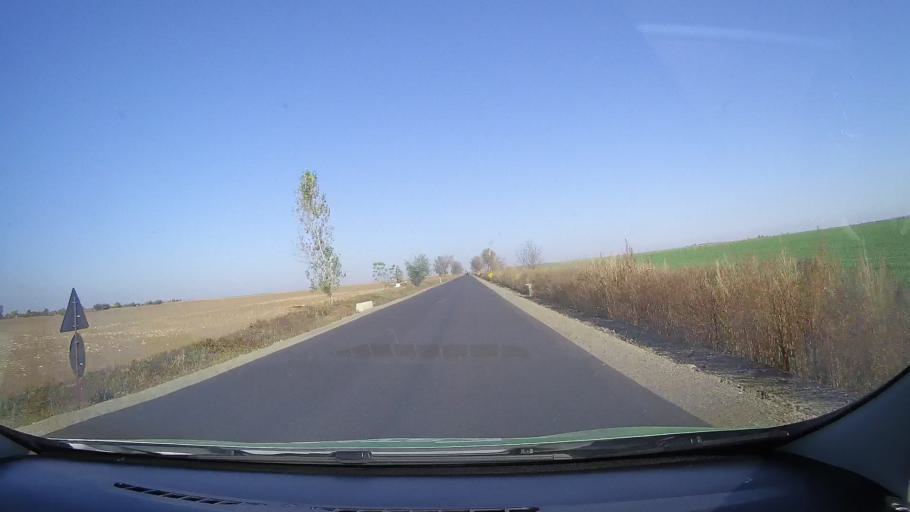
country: RO
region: Satu Mare
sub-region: Comuna Tiream
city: Tiream
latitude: 47.6241
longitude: 22.4680
